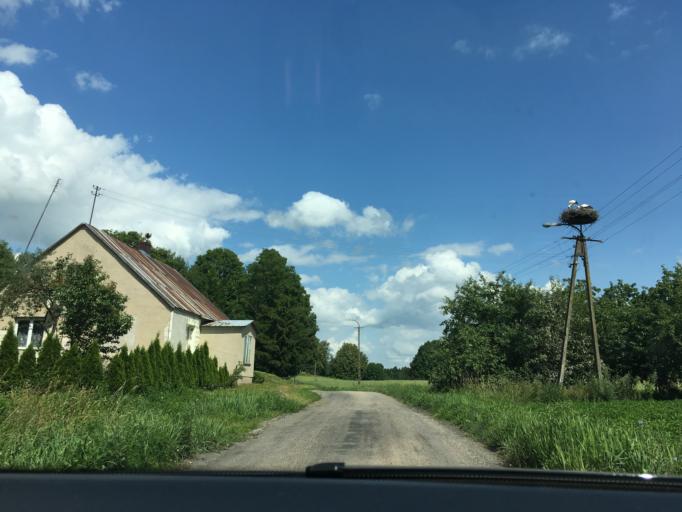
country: PL
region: Podlasie
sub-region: Powiat sejnenski
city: Krasnopol
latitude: 54.0912
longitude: 23.2634
